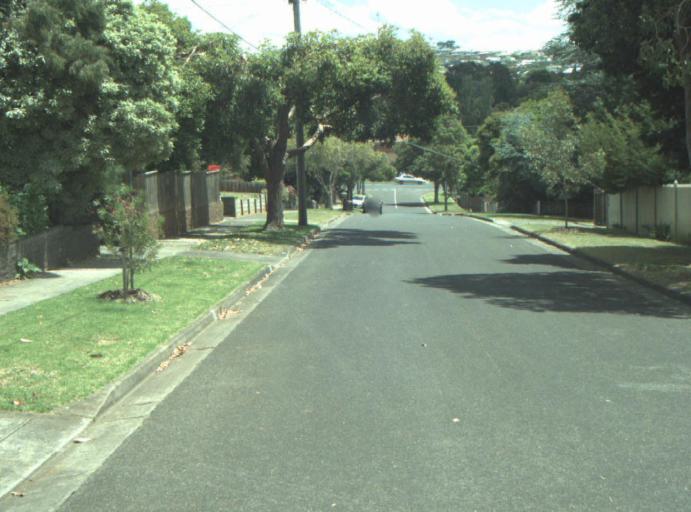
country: AU
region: Victoria
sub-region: Greater Geelong
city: Wandana Heights
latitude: -38.1762
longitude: 144.3196
